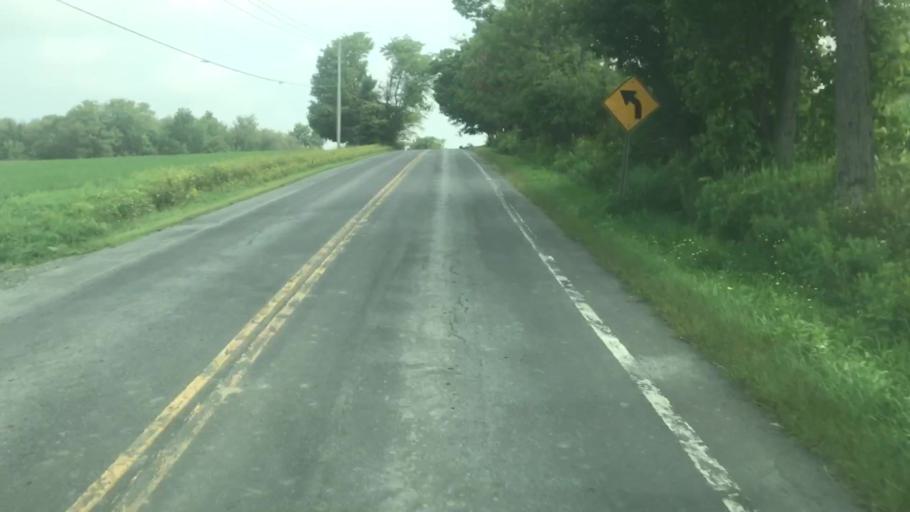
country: US
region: New York
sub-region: Onondaga County
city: Skaneateles
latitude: 42.8722
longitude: -76.4467
